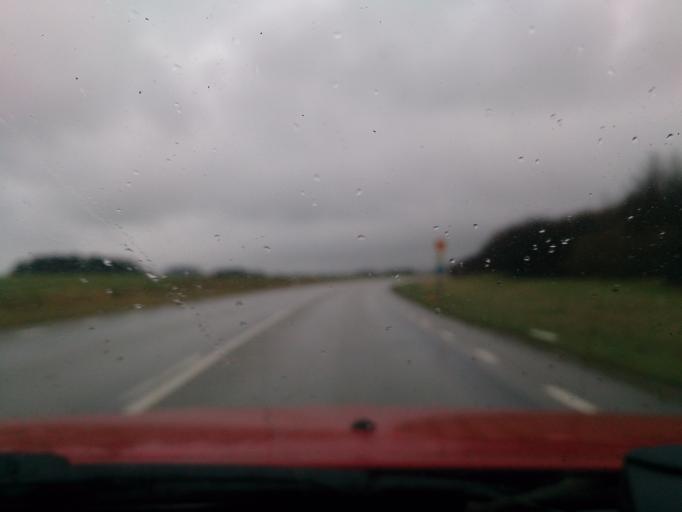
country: SE
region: Skane
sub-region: Ystads Kommun
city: Ystad
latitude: 55.4320
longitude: 13.7750
